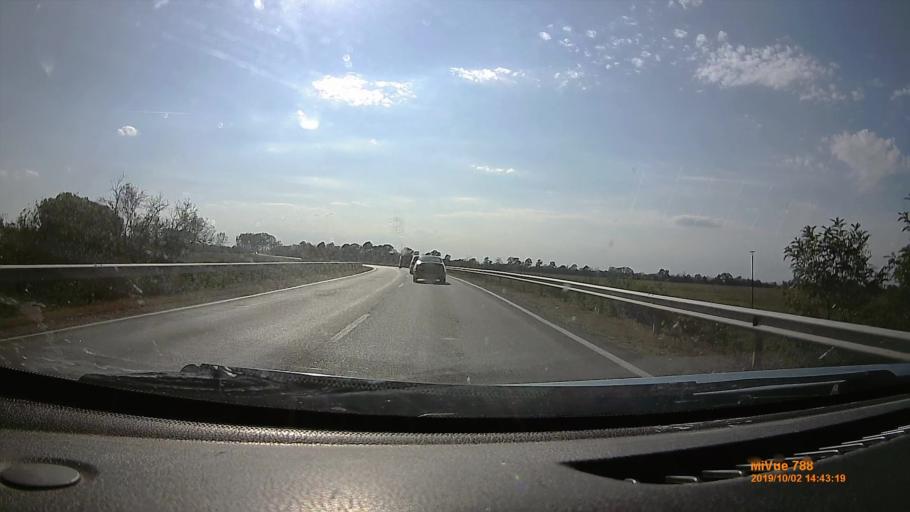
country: HU
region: Heves
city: Szihalom
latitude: 47.7755
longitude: 20.4658
